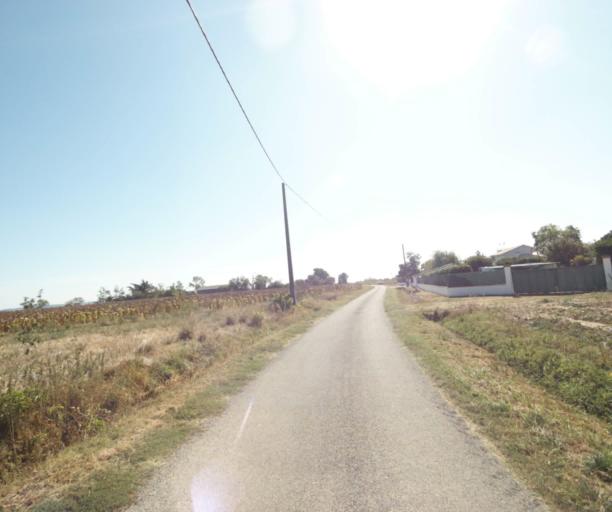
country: FR
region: Midi-Pyrenees
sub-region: Departement du Tarn-et-Garonne
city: Verdun-sur-Garonne
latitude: 43.8182
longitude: 1.2210
